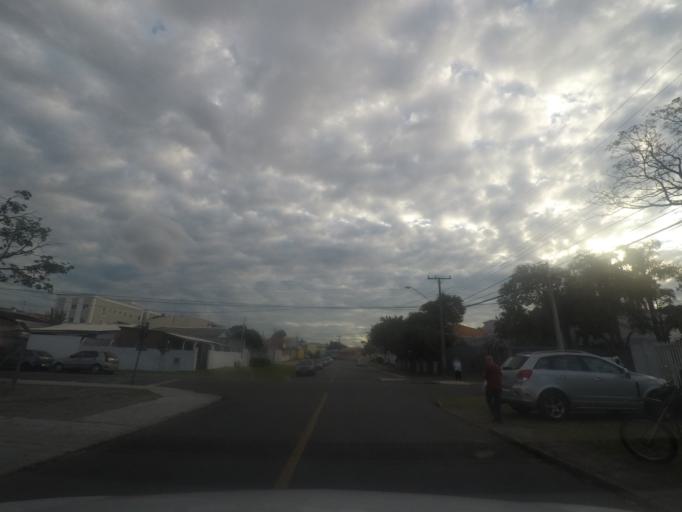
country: BR
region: Parana
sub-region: Pinhais
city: Pinhais
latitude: -25.4668
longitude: -49.2101
